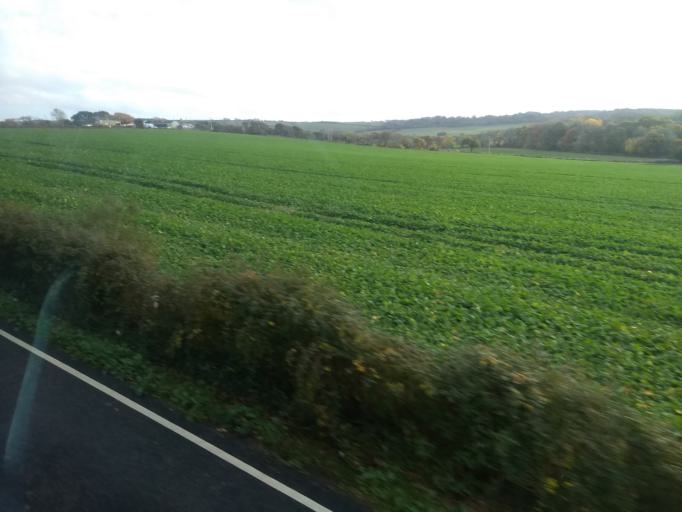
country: GB
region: England
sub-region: Isle of Wight
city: Shalfleet
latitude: 50.7031
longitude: -1.3643
